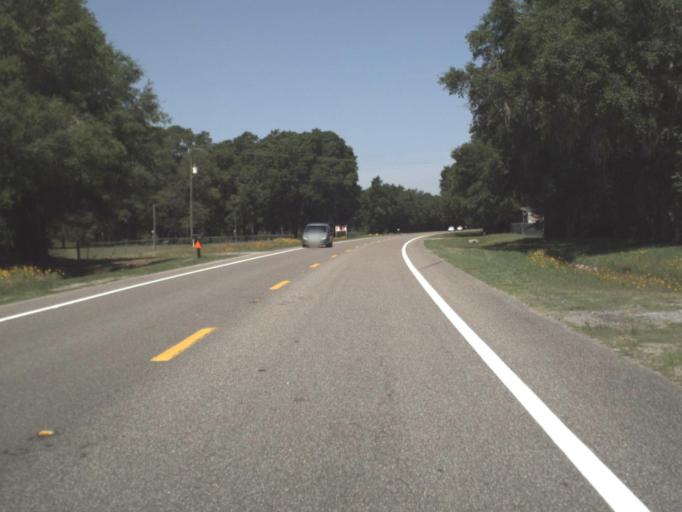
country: US
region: Florida
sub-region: Suwannee County
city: Wellborn
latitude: 30.2042
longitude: -82.8004
